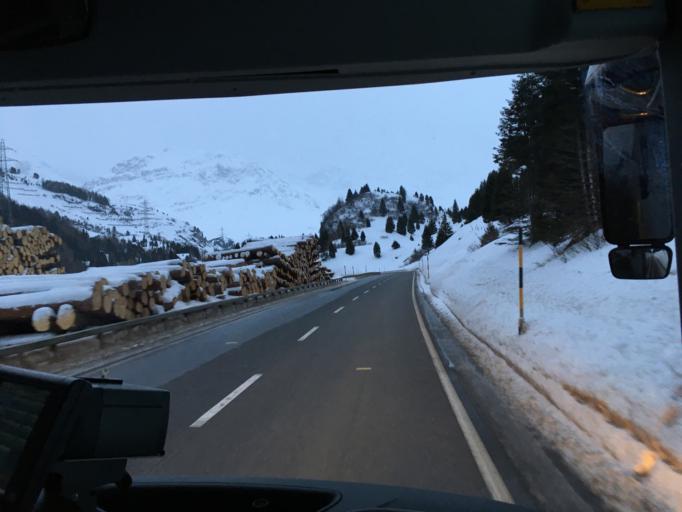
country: CH
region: Grisons
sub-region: Maloja District
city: Silvaplana
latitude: 46.4754
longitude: 9.6466
